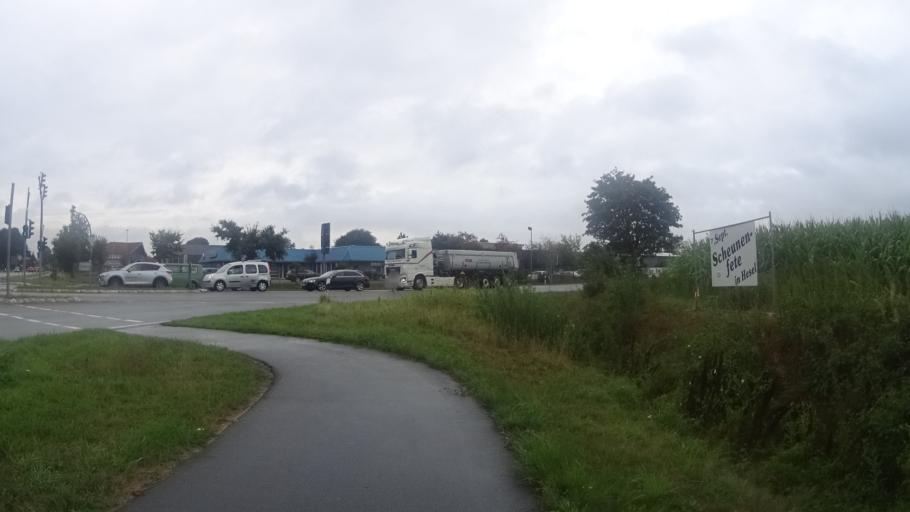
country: DE
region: Lower Saxony
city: Hesel
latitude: 53.2989
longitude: 7.5919
